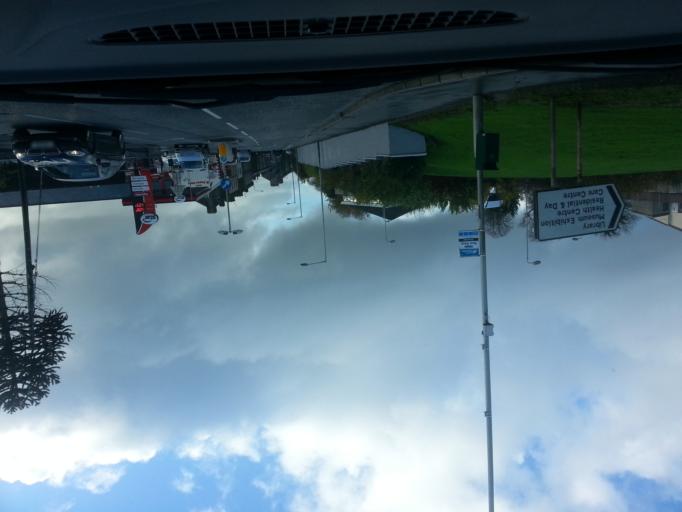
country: GB
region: Northern Ireland
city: Lisnaskea
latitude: 54.2562
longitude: -7.4483
